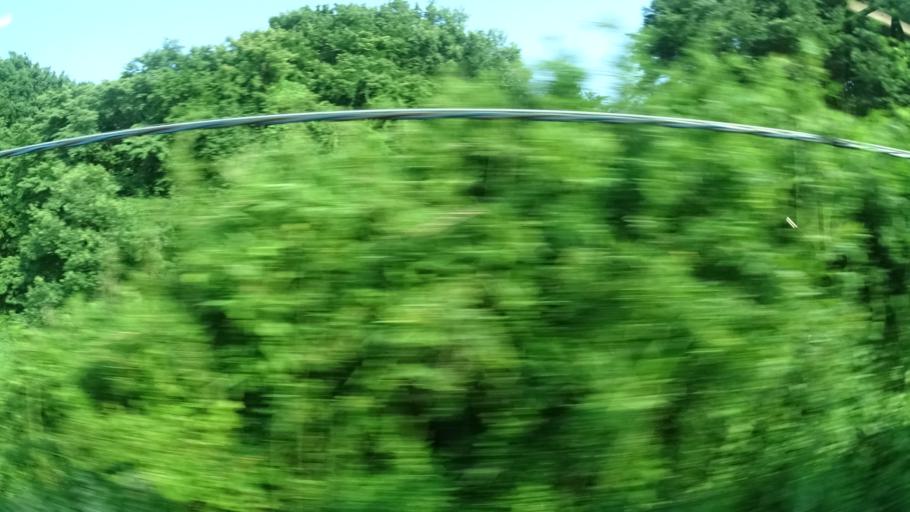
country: JP
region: Fukushima
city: Iwaki
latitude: 36.9470
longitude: 140.8341
